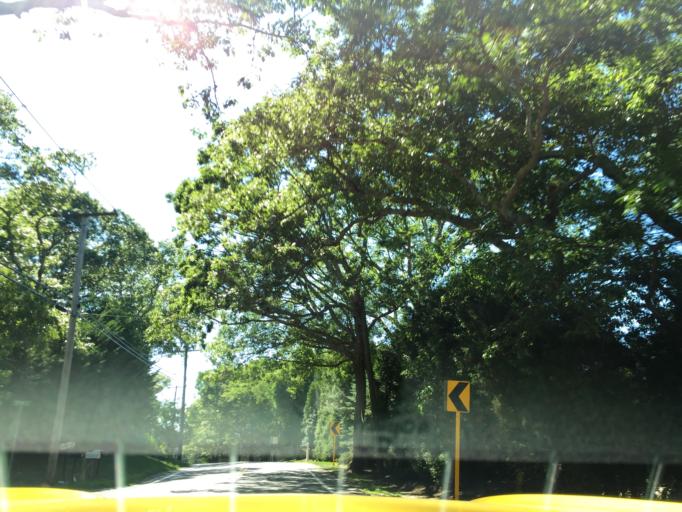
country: US
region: New York
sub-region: Suffolk County
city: Noyack
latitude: 40.9957
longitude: -72.3359
